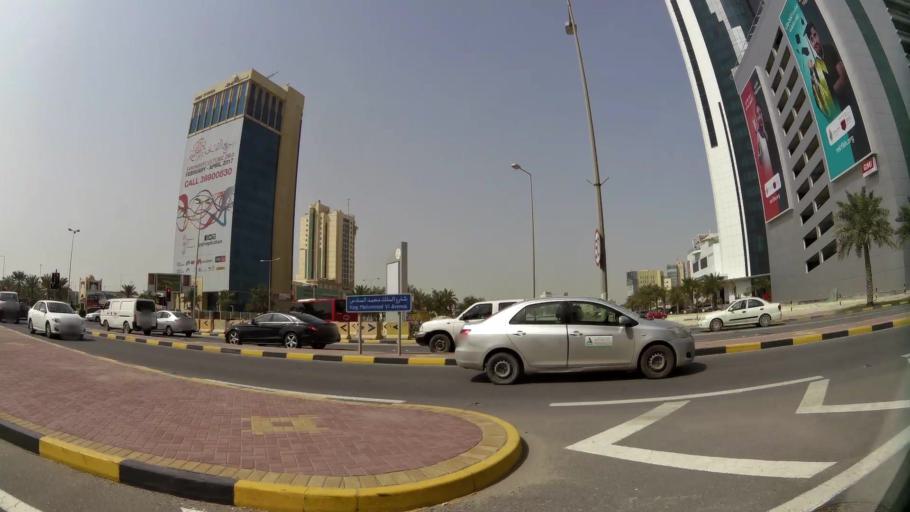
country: BH
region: Manama
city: Jidd Hafs
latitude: 26.2351
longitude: 50.5372
